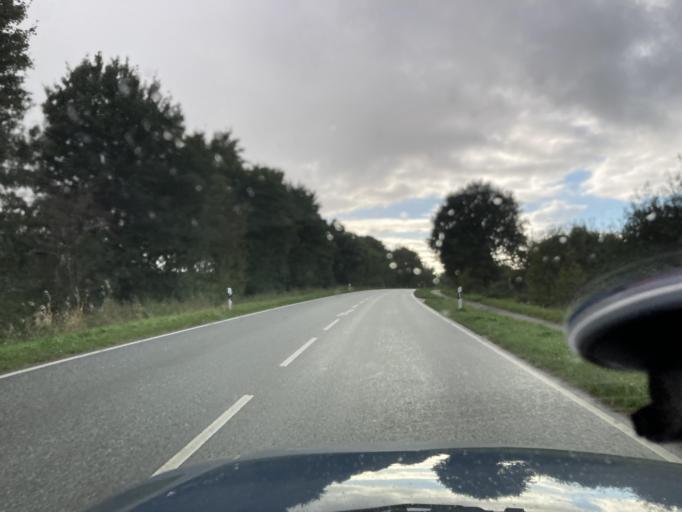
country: DE
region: Schleswig-Holstein
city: Suderdorf
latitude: 54.2186
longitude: 9.3369
